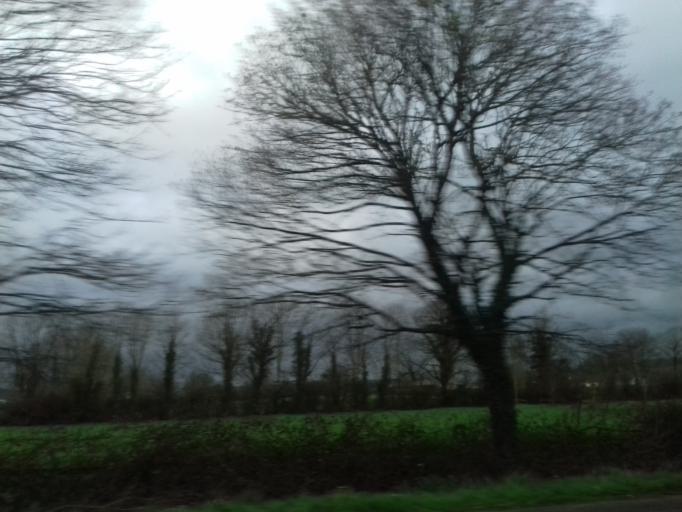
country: IE
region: Munster
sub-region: County Limerick
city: Newcastle West
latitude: 52.4439
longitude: -9.0753
